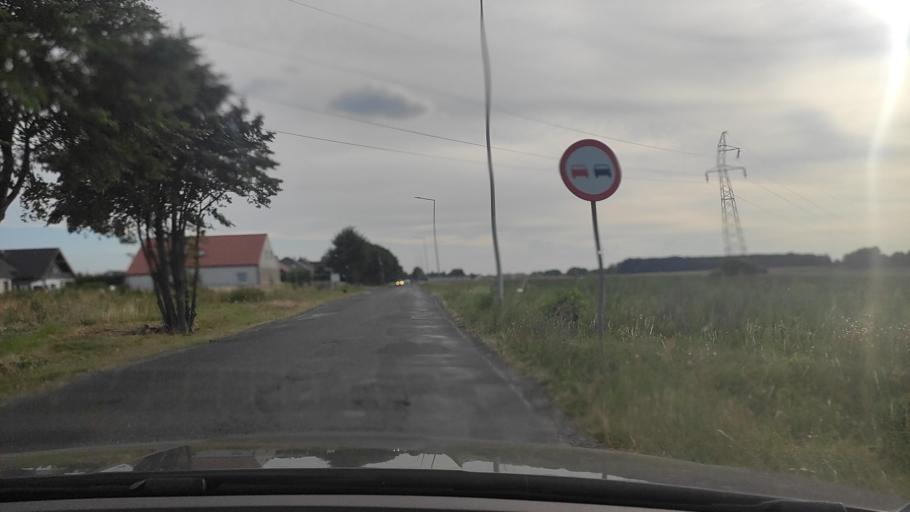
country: PL
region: Greater Poland Voivodeship
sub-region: Powiat poznanski
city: Kleszczewo
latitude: 52.3773
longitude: 17.1640
